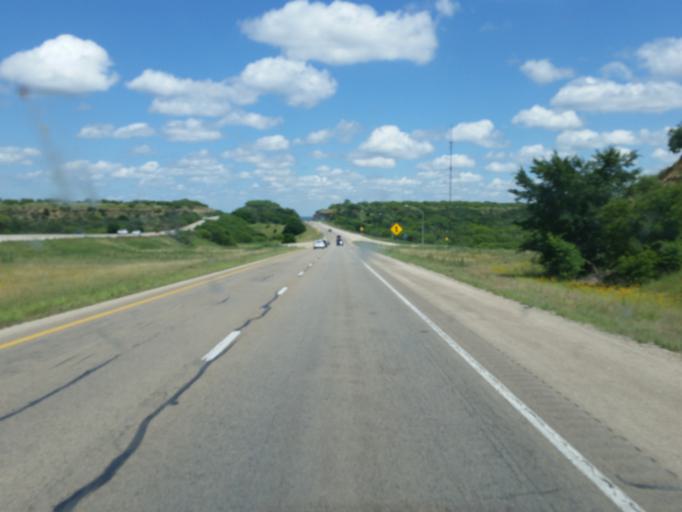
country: US
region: Texas
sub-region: Callahan County
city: Baird
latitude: 32.3973
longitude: -99.3707
